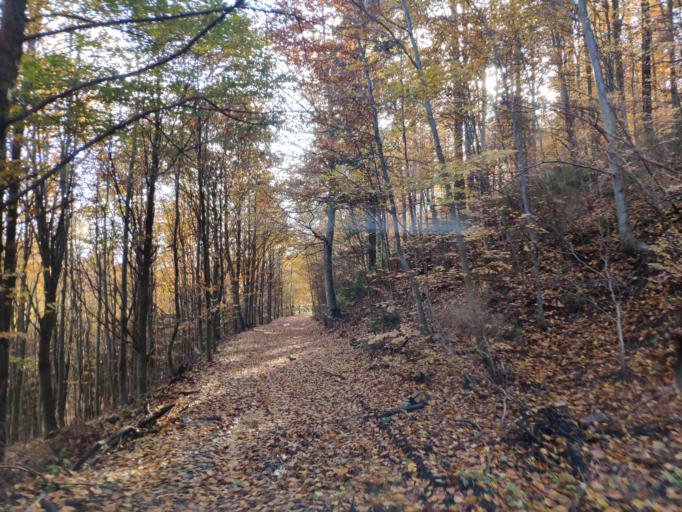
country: SK
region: Kosicky
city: Moldava nad Bodvou
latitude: 48.7402
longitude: 21.0194
